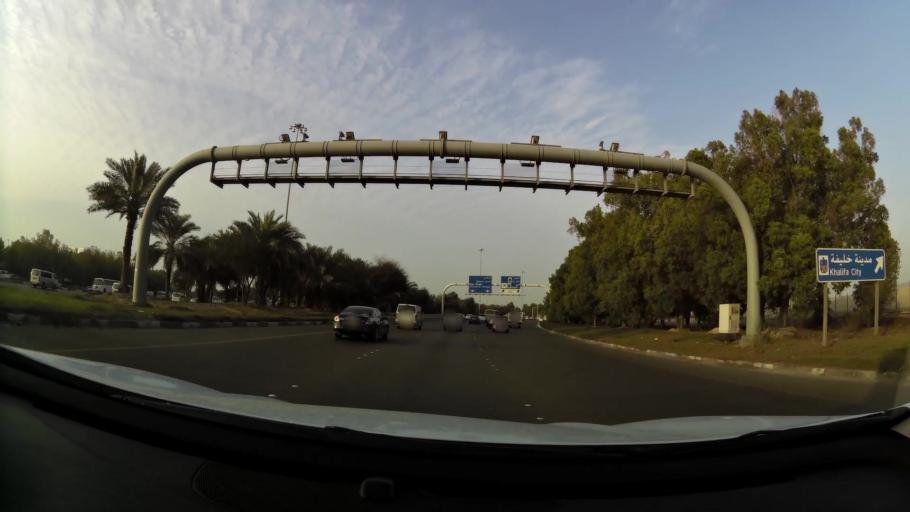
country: AE
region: Abu Dhabi
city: Abu Dhabi
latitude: 24.3876
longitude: 54.5246
